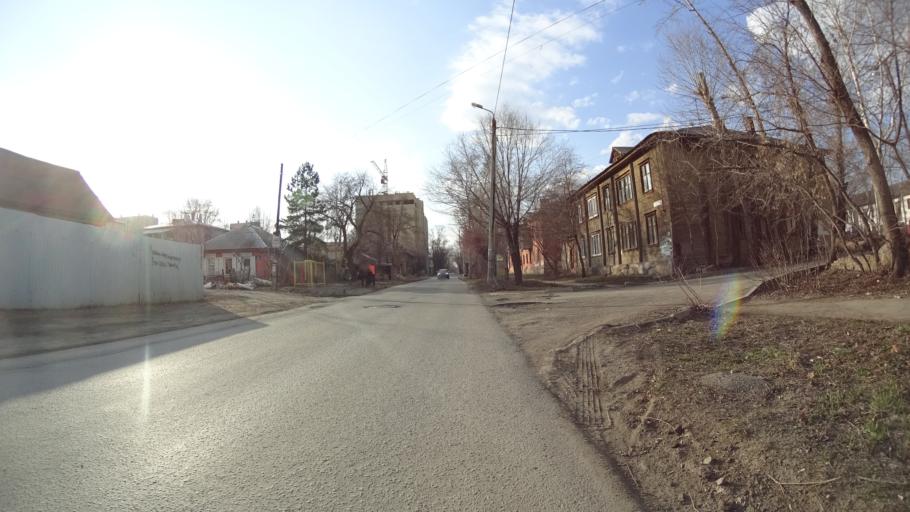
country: RU
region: Chelyabinsk
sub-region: Gorod Chelyabinsk
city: Chelyabinsk
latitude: 55.1405
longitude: 61.3878
